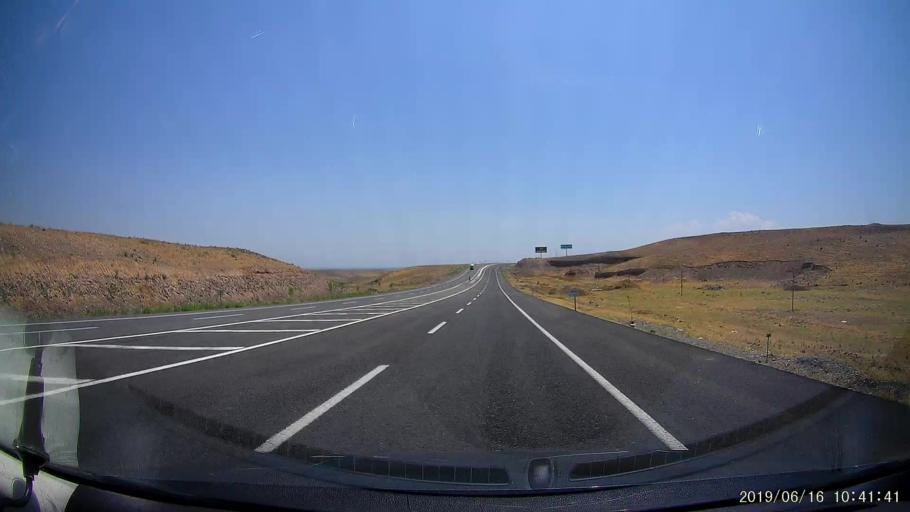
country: TR
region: Igdir
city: Tuzluca
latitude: 40.0466
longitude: 43.7893
